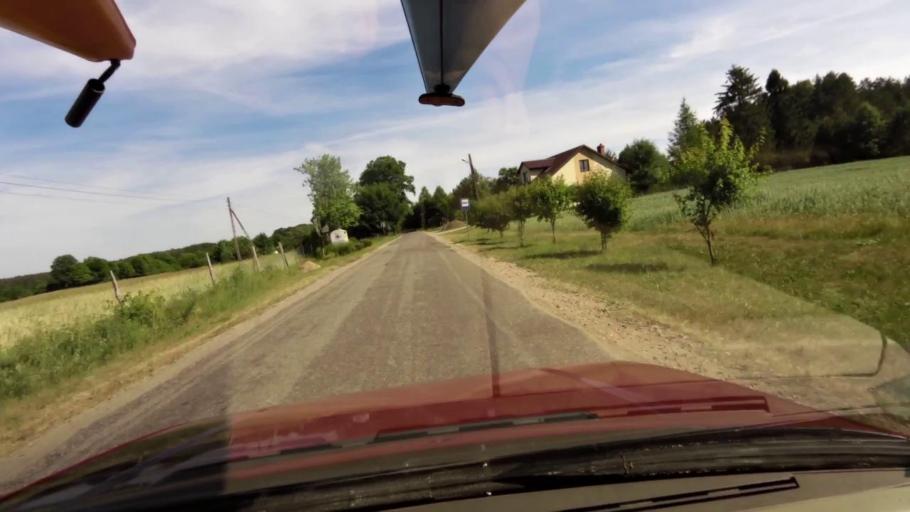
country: PL
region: Pomeranian Voivodeship
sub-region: Powiat slupski
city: Kepice
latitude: 54.1500
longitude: 16.9088
